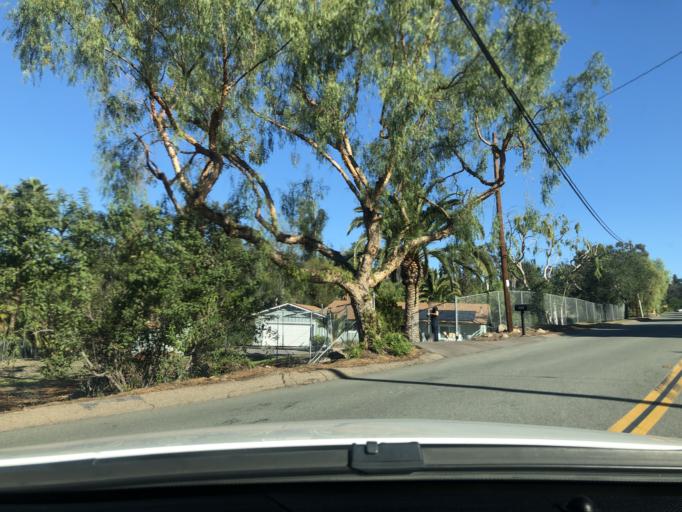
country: US
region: California
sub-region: San Diego County
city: Rancho San Diego
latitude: 32.7751
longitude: -116.9380
